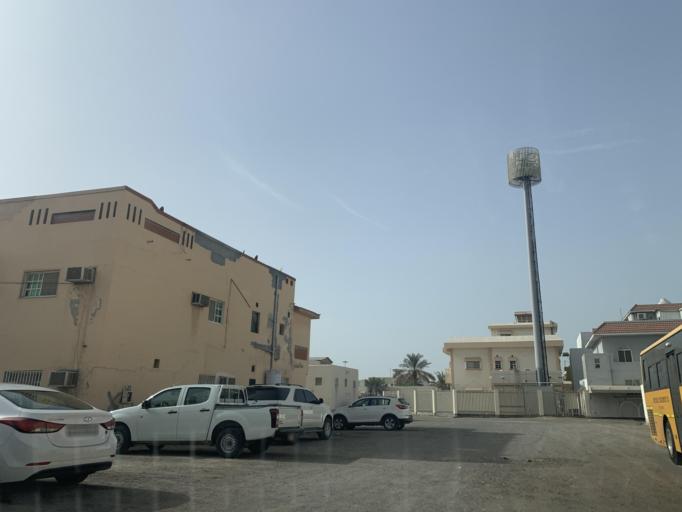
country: BH
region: Northern
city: Madinat `Isa
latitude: 26.1617
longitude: 50.5185
